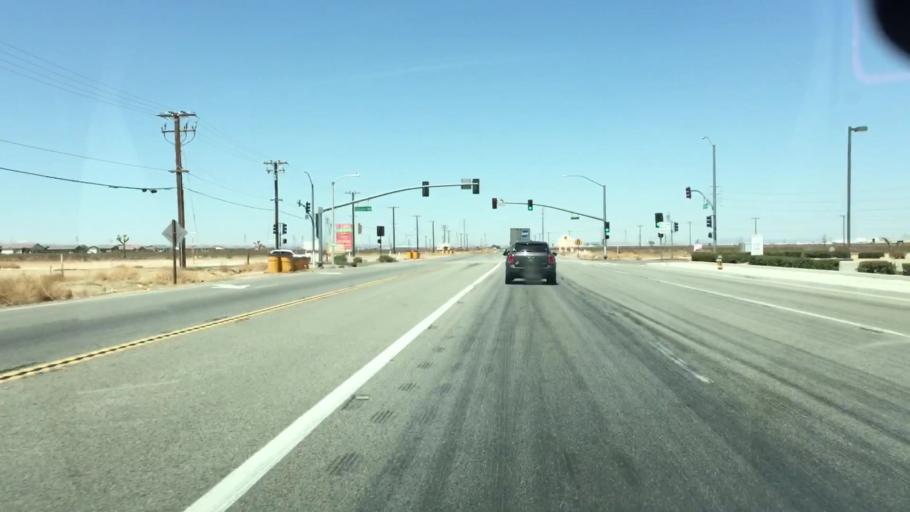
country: US
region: California
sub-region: San Bernardino County
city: Adelanto
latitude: 34.5350
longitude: -117.3994
